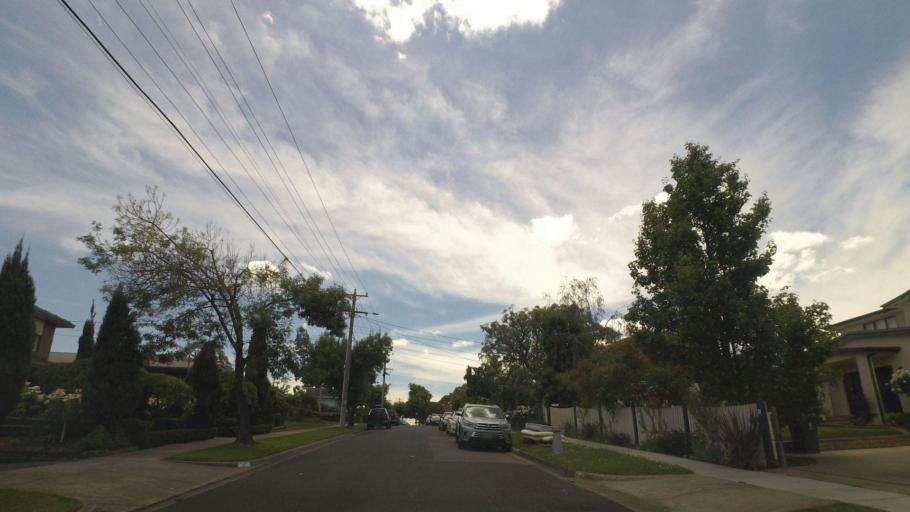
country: AU
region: Victoria
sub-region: Knox
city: Wantirna
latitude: -37.8391
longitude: 145.2095
